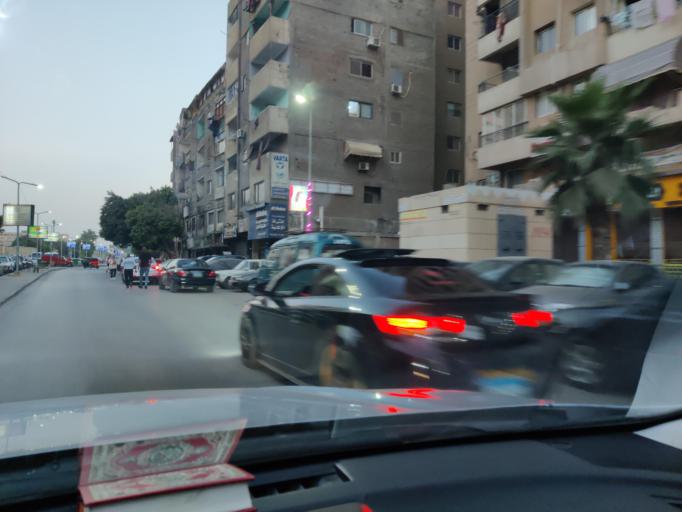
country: EG
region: Muhafazat al Qahirah
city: Cairo
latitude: 30.1085
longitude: 31.3036
